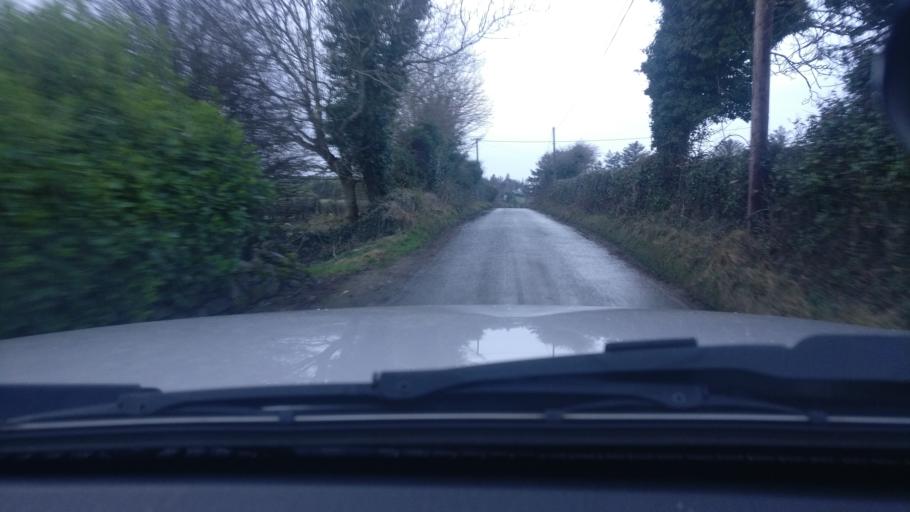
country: IE
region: Connaught
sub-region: County Galway
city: Loughrea
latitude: 53.1639
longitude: -8.5446
